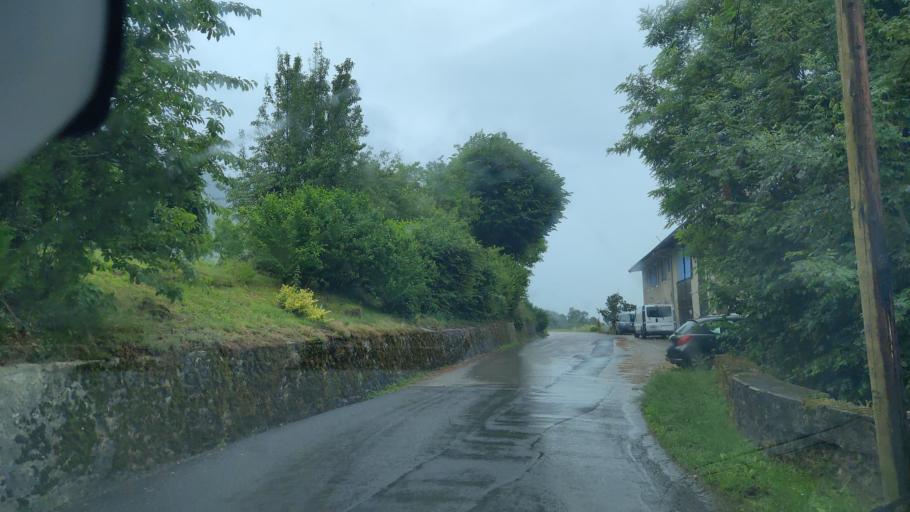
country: FR
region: Rhone-Alpes
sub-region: Departement de la Savoie
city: Chindrieux
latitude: 45.8329
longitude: 5.8473
